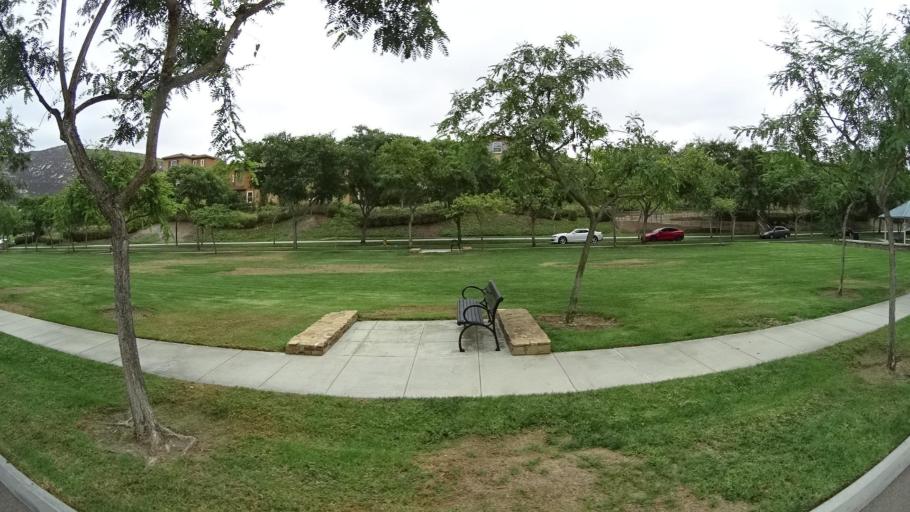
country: US
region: California
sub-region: San Diego County
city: Fairbanks Ranch
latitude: 33.0251
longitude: -117.1110
